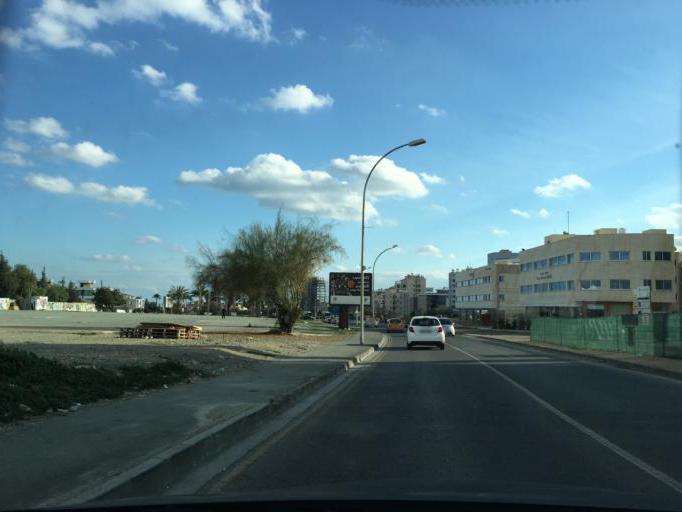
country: CY
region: Limassol
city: Limassol
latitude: 34.6963
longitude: 33.0650
